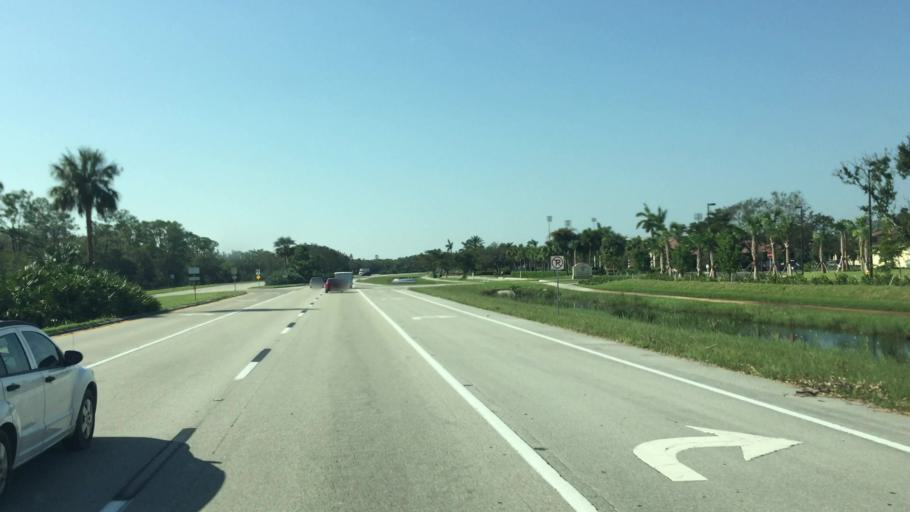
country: US
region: Florida
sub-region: Lee County
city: Villas
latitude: 26.5436
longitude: -81.8396
